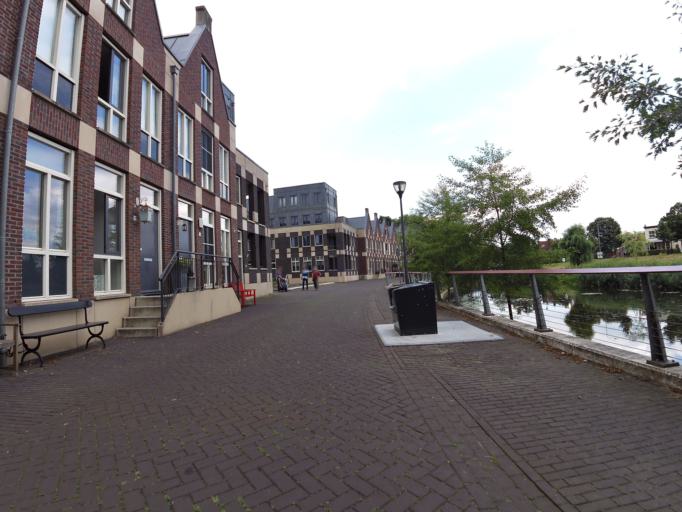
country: NL
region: Gelderland
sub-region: Gemeente Doesburg
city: Doesburg
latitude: 52.0135
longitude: 6.1301
